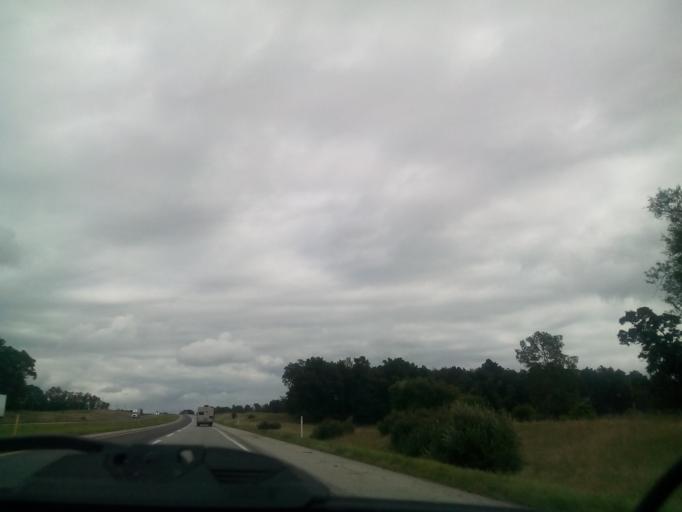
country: US
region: Michigan
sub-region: Saint Joseph County
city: Sturgis
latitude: 41.7410
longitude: -85.3051
